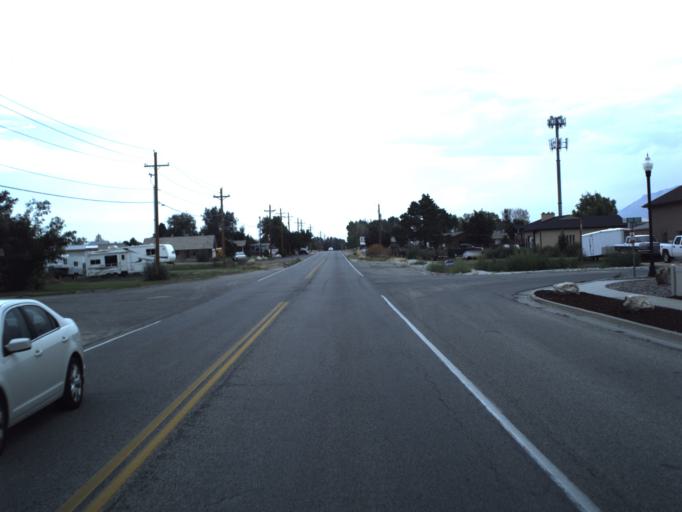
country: US
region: Utah
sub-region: Weber County
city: Hooper
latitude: 41.1933
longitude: -112.0931
